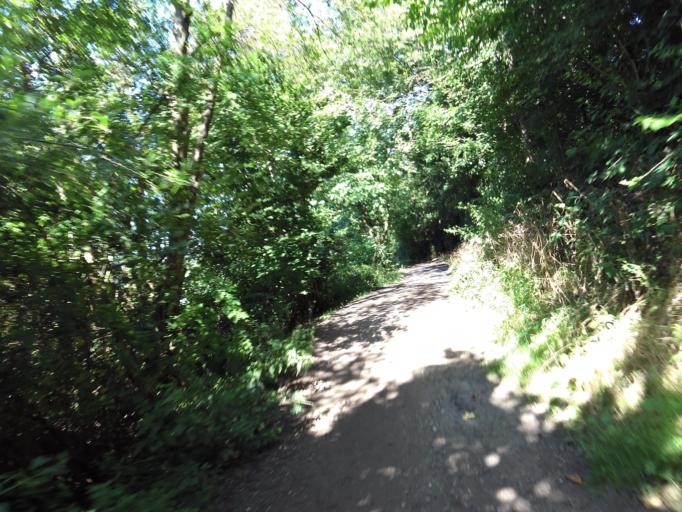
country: DE
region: North Rhine-Westphalia
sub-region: Regierungsbezirk Koln
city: Herzogenrath
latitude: 50.8665
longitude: 6.1055
